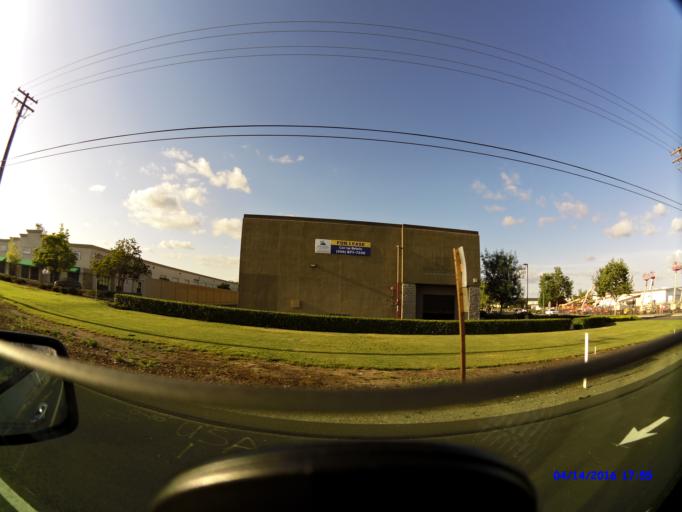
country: US
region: California
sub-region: Stanislaus County
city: Del Rio
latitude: 37.7113
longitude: -121.0029
